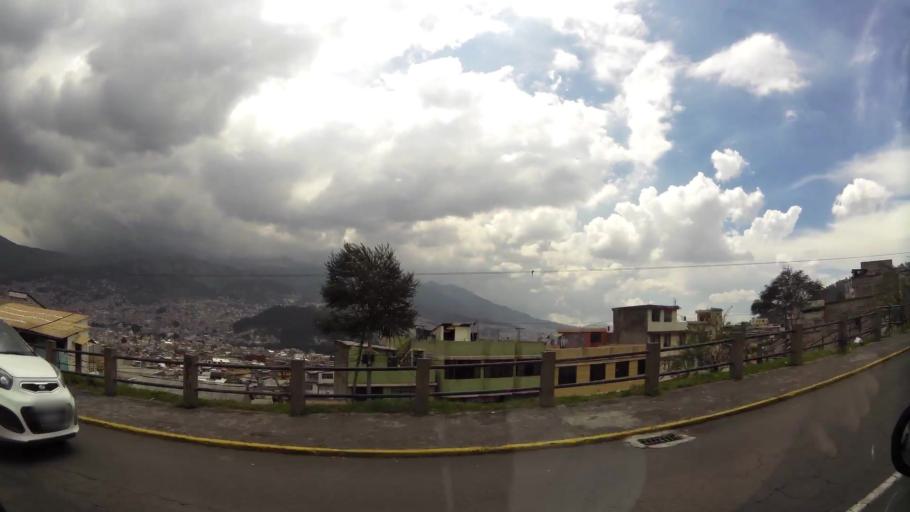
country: EC
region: Pichincha
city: Quito
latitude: -0.2492
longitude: -78.5099
